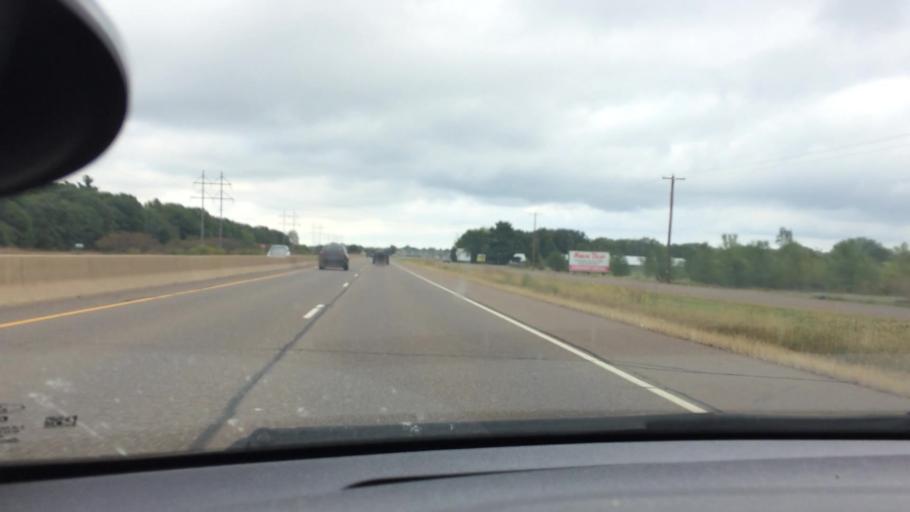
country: US
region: Wisconsin
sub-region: Chippewa County
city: Chippewa Falls
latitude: 44.9066
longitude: -91.4075
